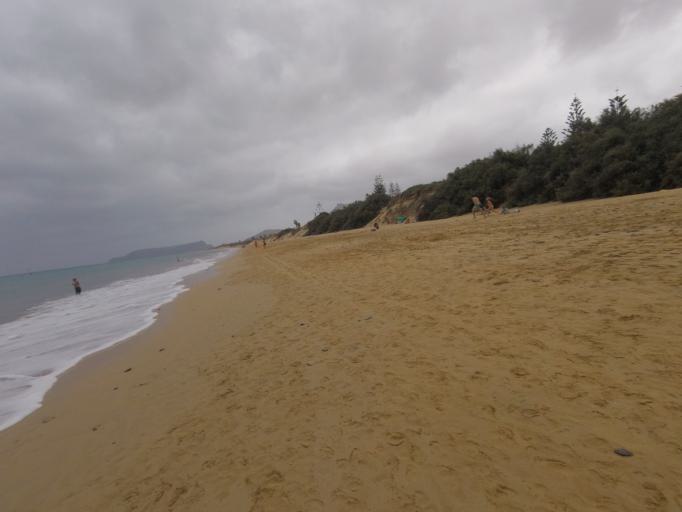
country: PT
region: Madeira
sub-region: Porto Santo
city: Vila de Porto Santo
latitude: 33.0553
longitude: -16.3384
